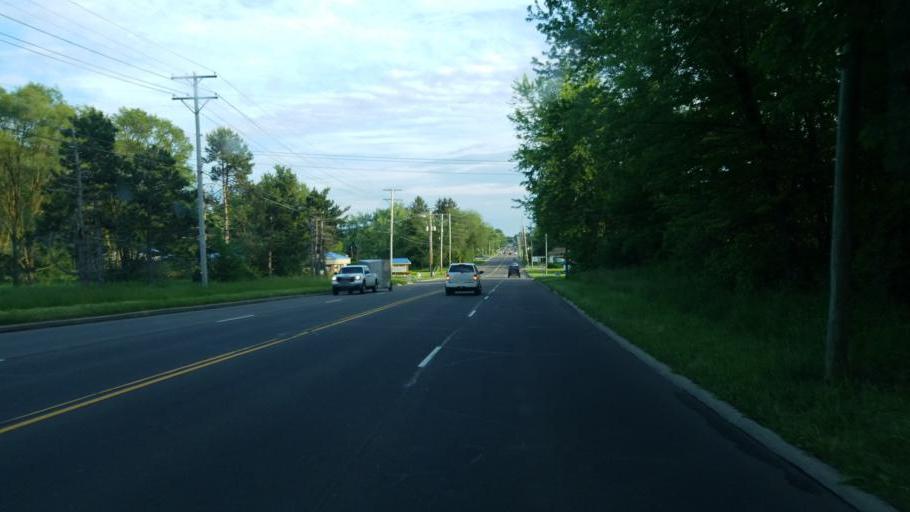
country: US
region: Ohio
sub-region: Stark County
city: Greentown
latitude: 40.9370
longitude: -81.4023
